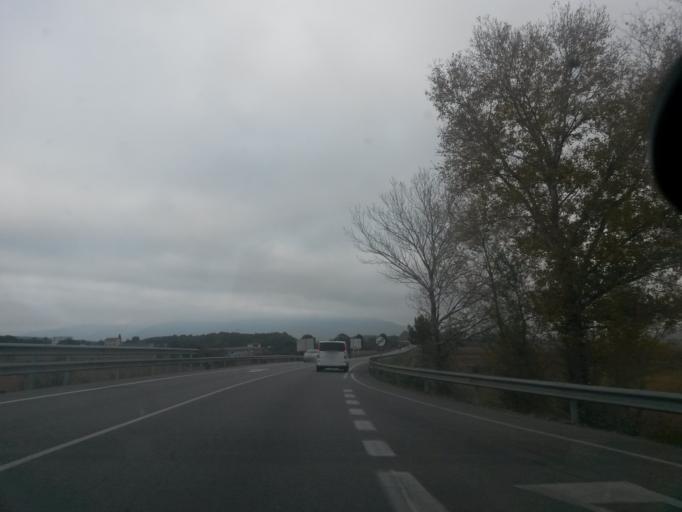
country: ES
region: Catalonia
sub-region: Provincia de Girona
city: Banyoles
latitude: 42.1410
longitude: 2.7638
